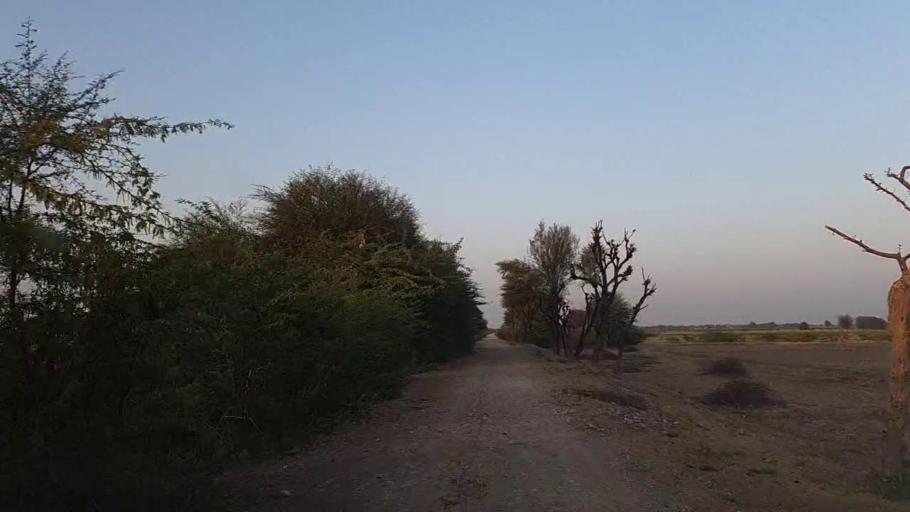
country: PK
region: Sindh
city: Naukot
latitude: 24.8725
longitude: 69.3485
